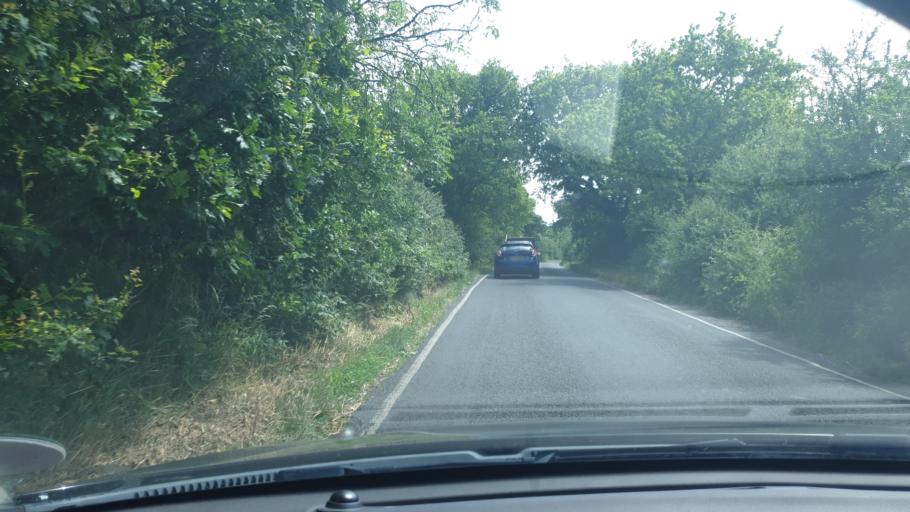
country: GB
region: England
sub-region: Essex
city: Clacton-on-Sea
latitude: 51.8120
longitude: 1.1794
